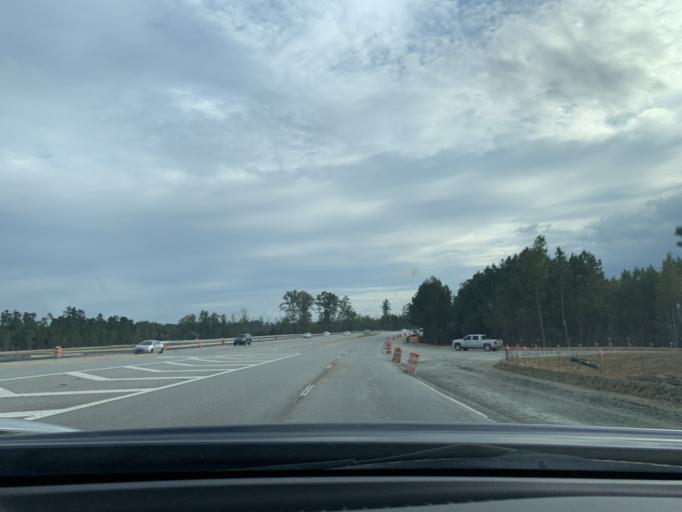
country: US
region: Georgia
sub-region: Chatham County
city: Pooler
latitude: 32.1076
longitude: -81.2664
